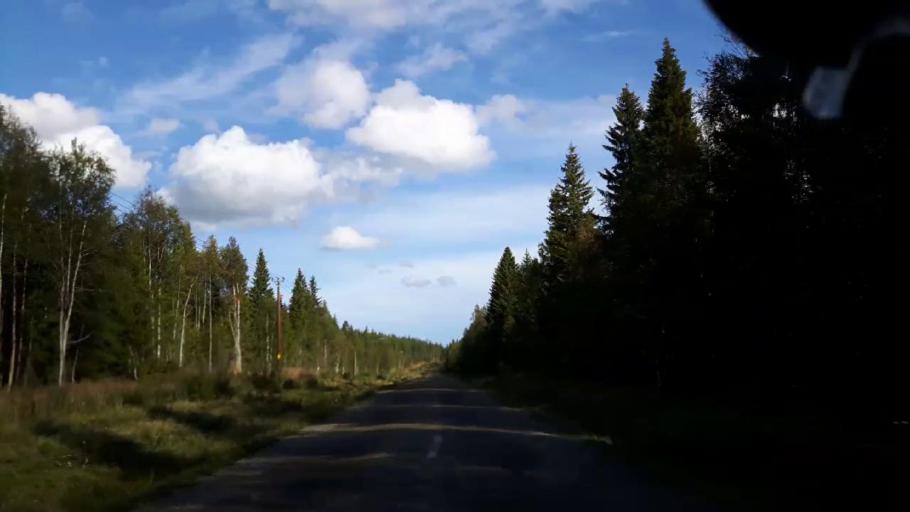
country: SE
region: Jaemtland
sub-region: Ragunda Kommun
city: Hammarstrand
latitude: 63.4357
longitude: 16.0219
